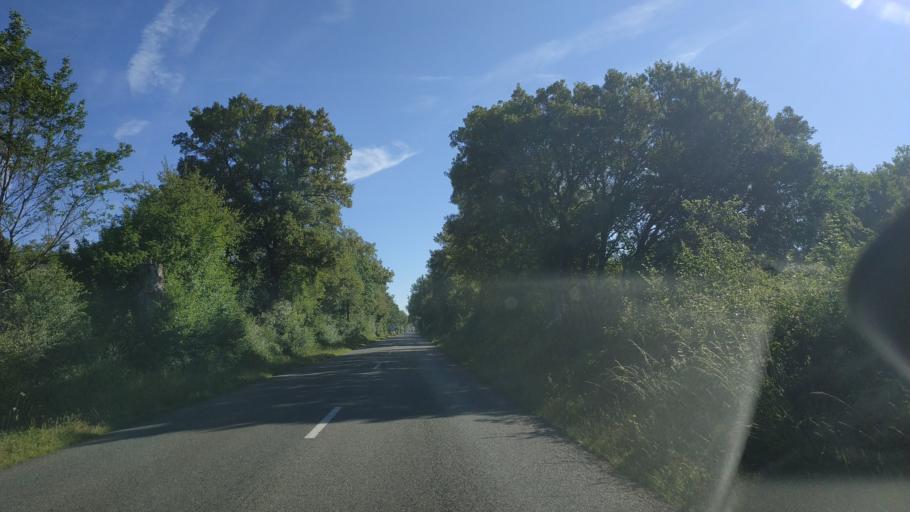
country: FR
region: Midi-Pyrenees
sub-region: Departement du Lot
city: Lacapelle-Marival
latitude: 44.6694
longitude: 1.8686
